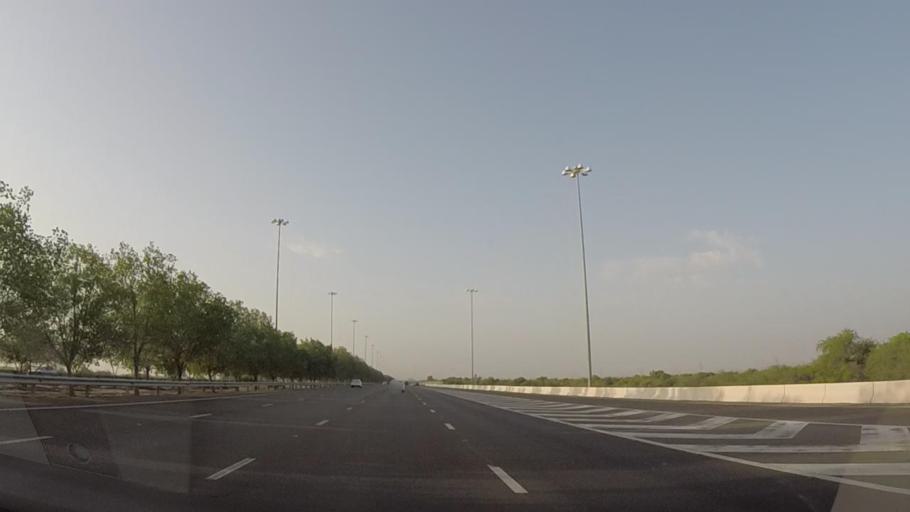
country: AE
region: Dubai
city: Dubai
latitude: 24.7948
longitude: 54.8612
